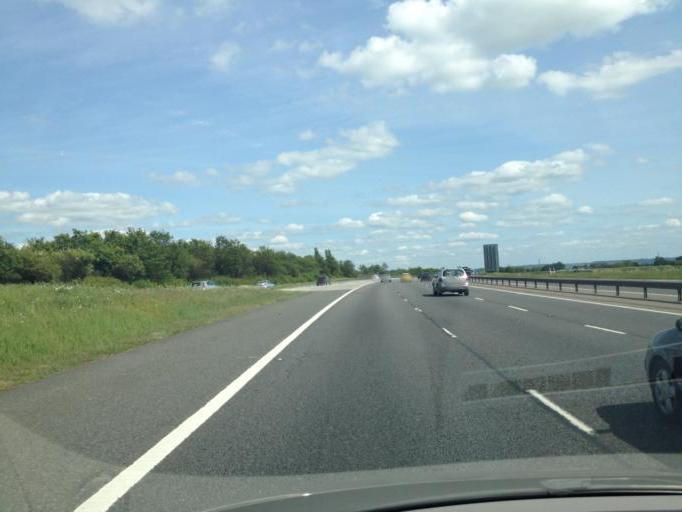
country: GB
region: England
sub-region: Oxfordshire
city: Wheatley
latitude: 51.7324
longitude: -1.0758
